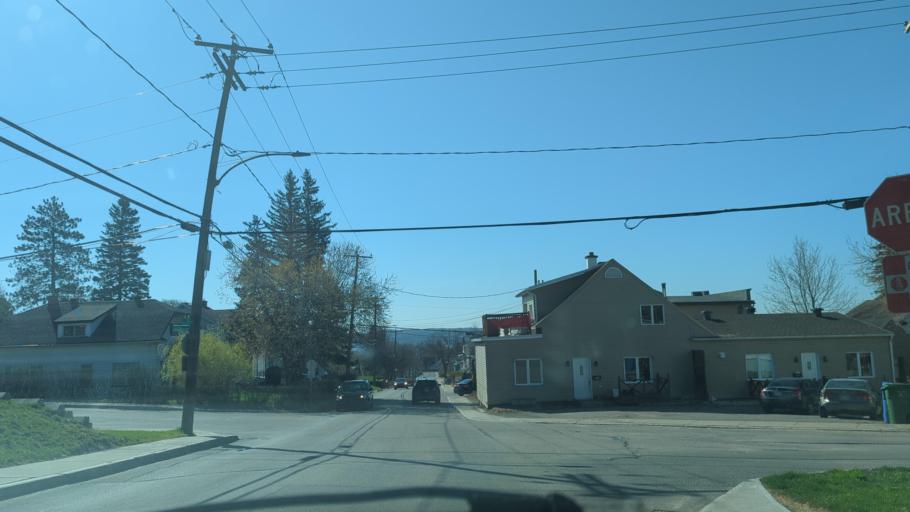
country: CA
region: Quebec
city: Quebec
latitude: 46.8539
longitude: -71.2144
